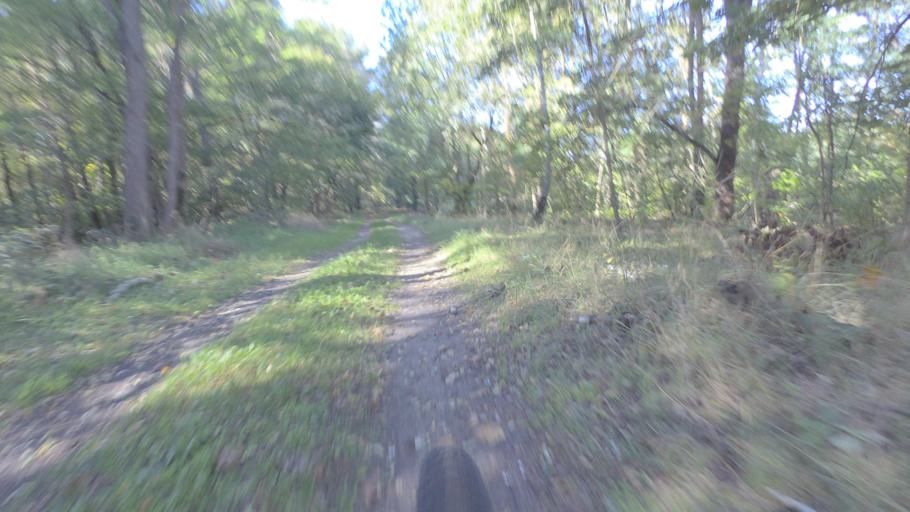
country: DE
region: Brandenburg
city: Sperenberg
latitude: 52.1437
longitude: 13.3512
